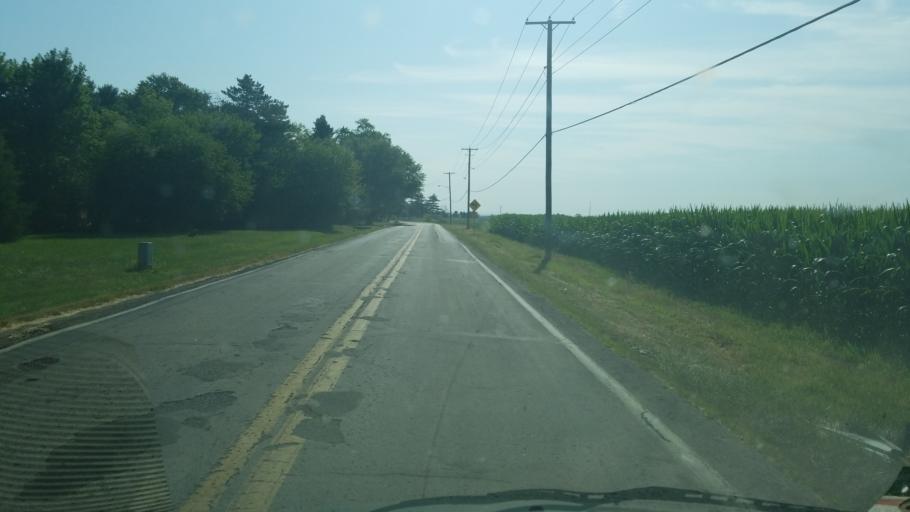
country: US
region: Ohio
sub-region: Franklin County
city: Grove City
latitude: 39.8264
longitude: -83.0947
